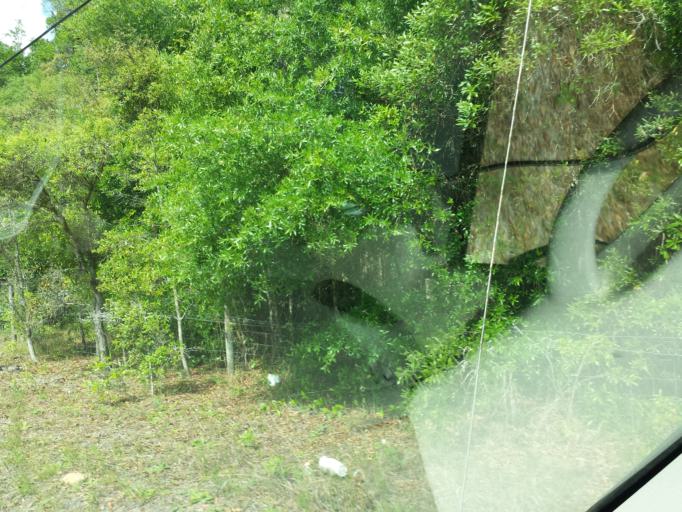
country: US
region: Florida
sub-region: Hernando County
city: Hill 'n Dale
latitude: 28.5319
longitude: -82.2842
